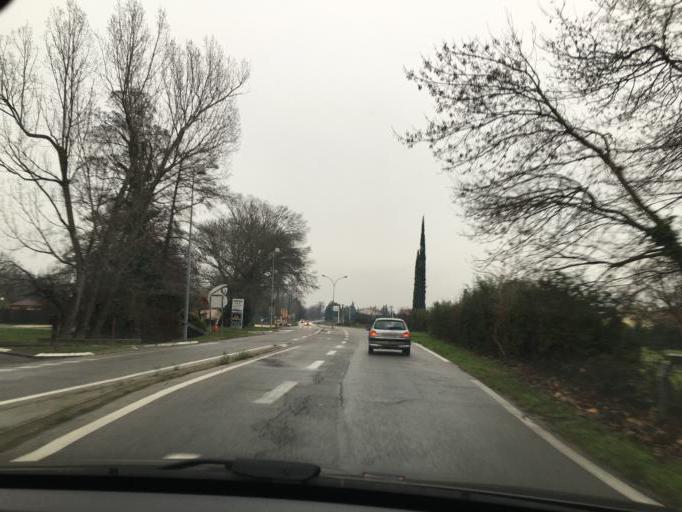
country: FR
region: Provence-Alpes-Cote d'Azur
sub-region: Departement du Vaucluse
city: L'Isle-sur-la-Sorgue
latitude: 43.9144
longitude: 5.0708
